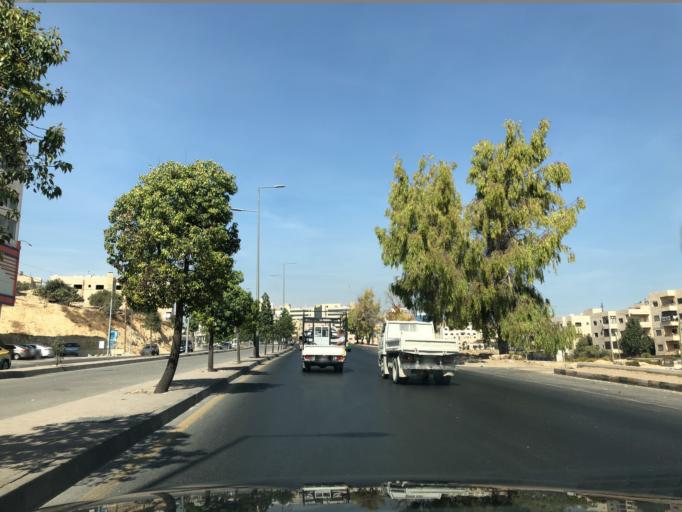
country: JO
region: Amman
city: Al Jubayhah
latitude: 32.0227
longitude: 35.8602
